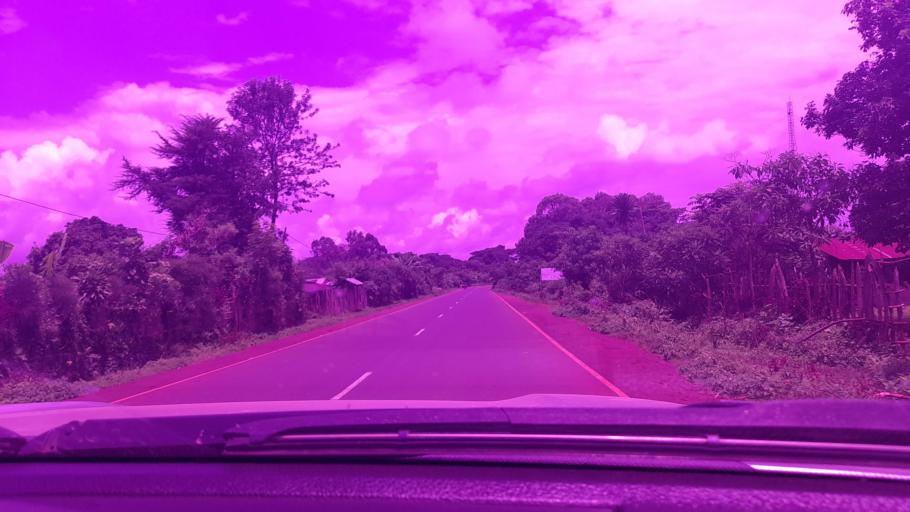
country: ET
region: Oromiya
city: Metu
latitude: 8.3398
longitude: 35.7202
